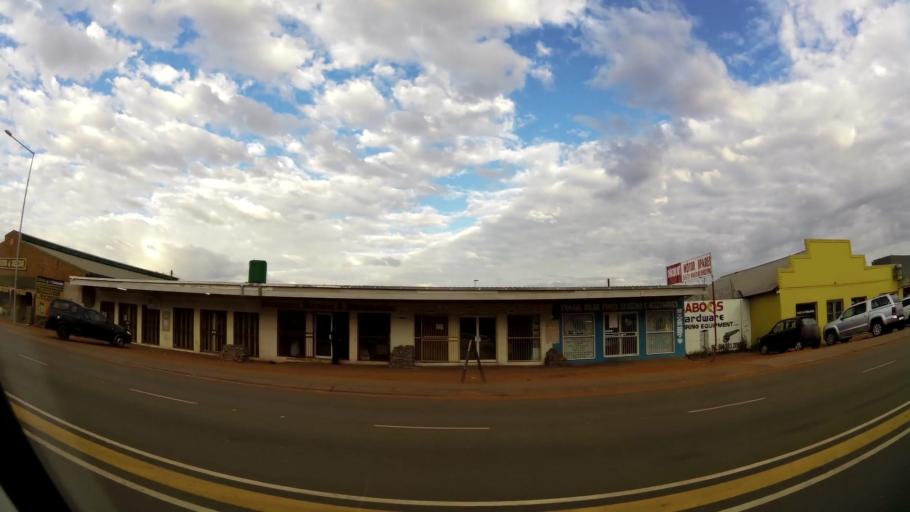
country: ZA
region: Limpopo
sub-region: Waterberg District Municipality
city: Modimolle
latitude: -24.5167
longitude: 28.7171
